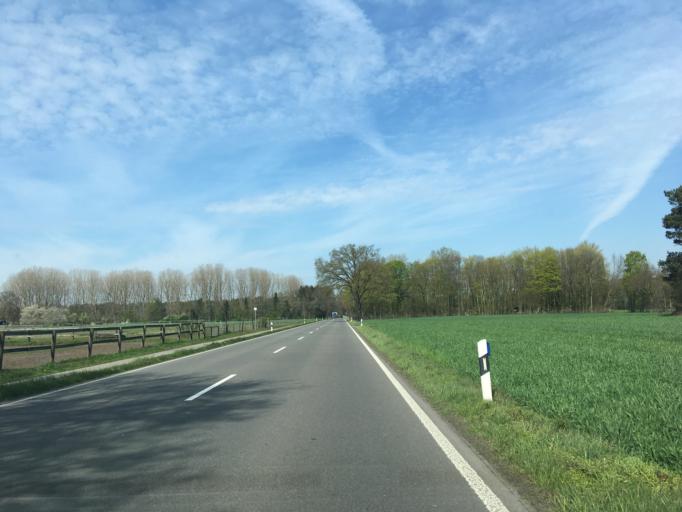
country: DE
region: North Rhine-Westphalia
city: Stadtlohn
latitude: 52.0045
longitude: 6.8709
